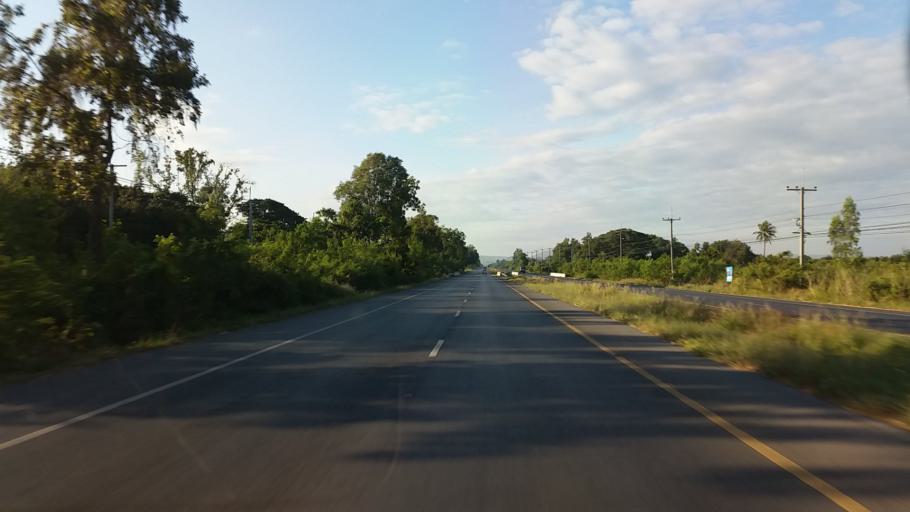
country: TH
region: Lop Buri
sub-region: Amphoe Tha Luang
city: Tha Luang
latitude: 15.0404
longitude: 100.9562
